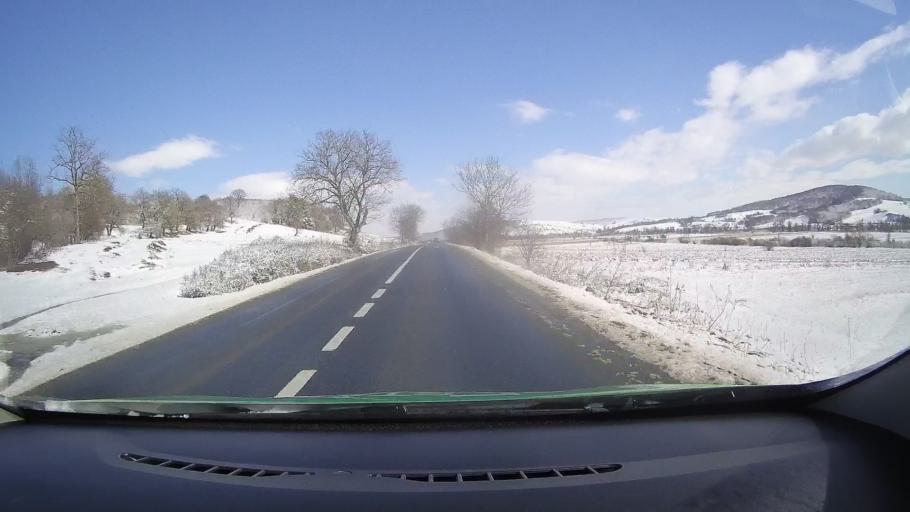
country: RO
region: Sibiu
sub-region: Comuna Nocrich
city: Nocrich
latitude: 45.8441
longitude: 24.4264
